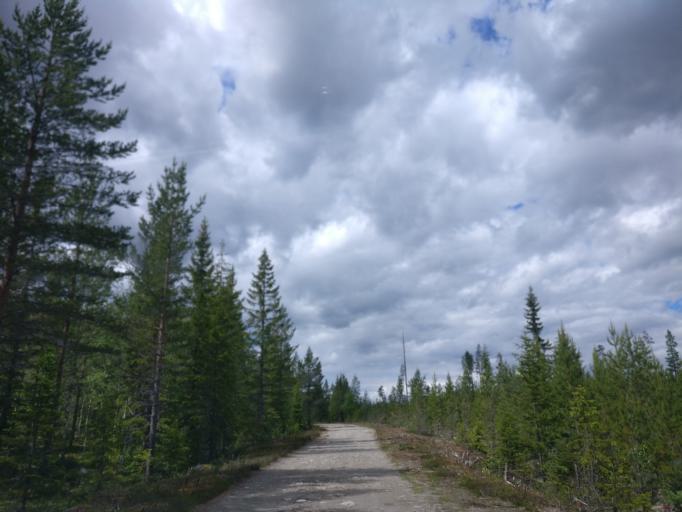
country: SE
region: Jaemtland
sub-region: Harjedalens Kommun
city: Sveg
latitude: 62.1958
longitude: 13.4139
